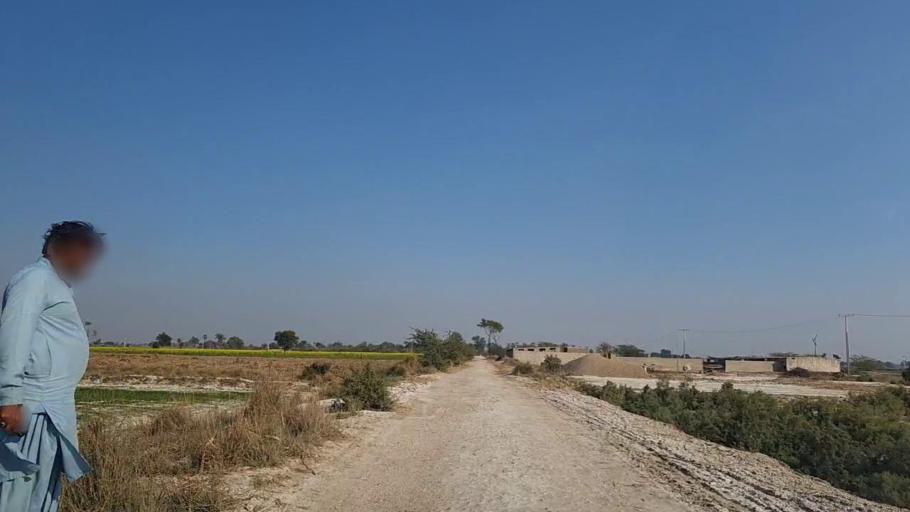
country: PK
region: Sindh
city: Bandhi
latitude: 26.5707
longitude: 68.3041
